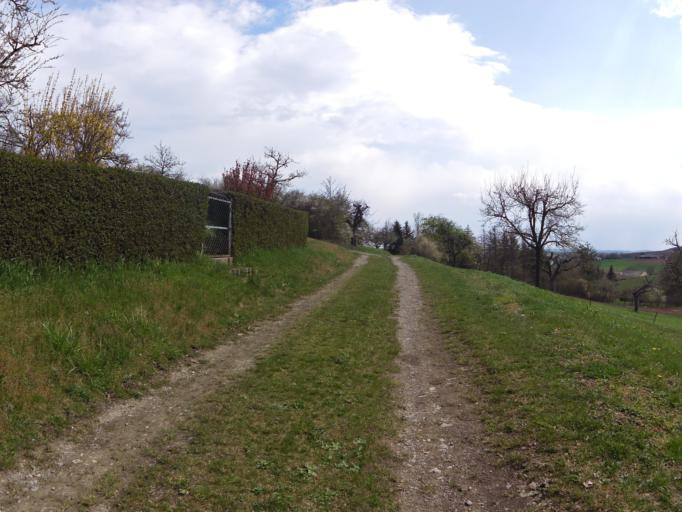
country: DE
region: Bavaria
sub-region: Regierungsbezirk Unterfranken
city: Rimpar
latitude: 49.8623
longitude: 9.9448
